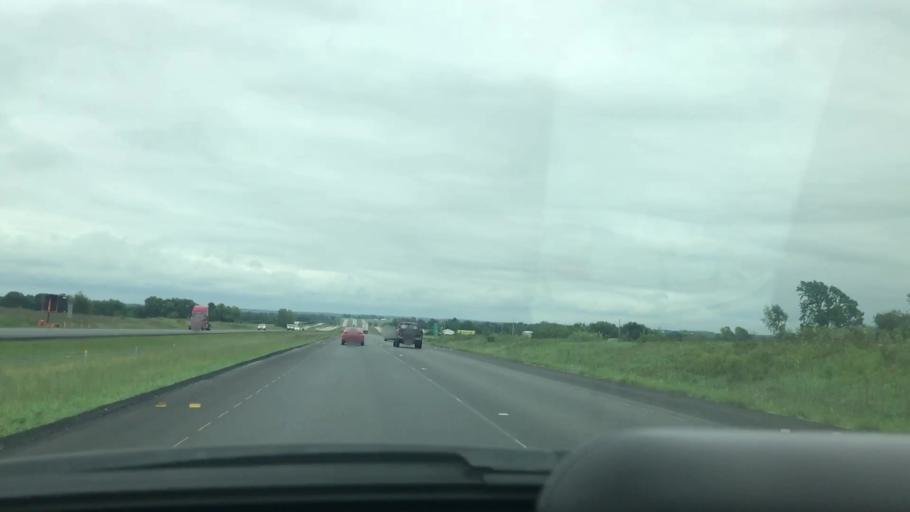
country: US
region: Missouri
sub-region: Lawrence County
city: Mount Vernon
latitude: 37.0746
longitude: -93.9243
